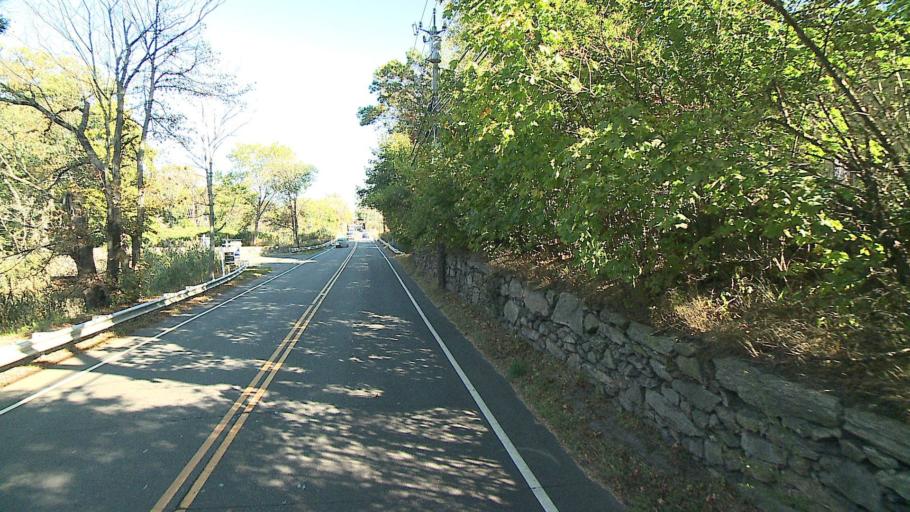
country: US
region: Connecticut
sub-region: Fairfield County
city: East Norwalk
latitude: 41.1160
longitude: -73.3758
